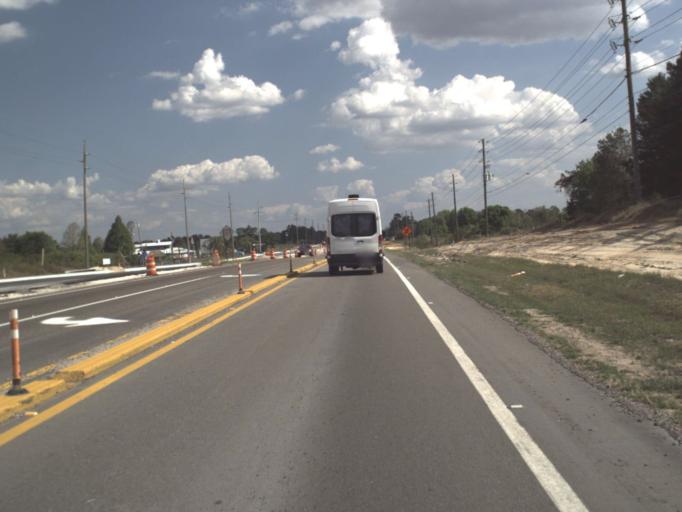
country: US
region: Florida
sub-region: Lake County
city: Four Corners
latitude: 28.4223
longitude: -81.7079
